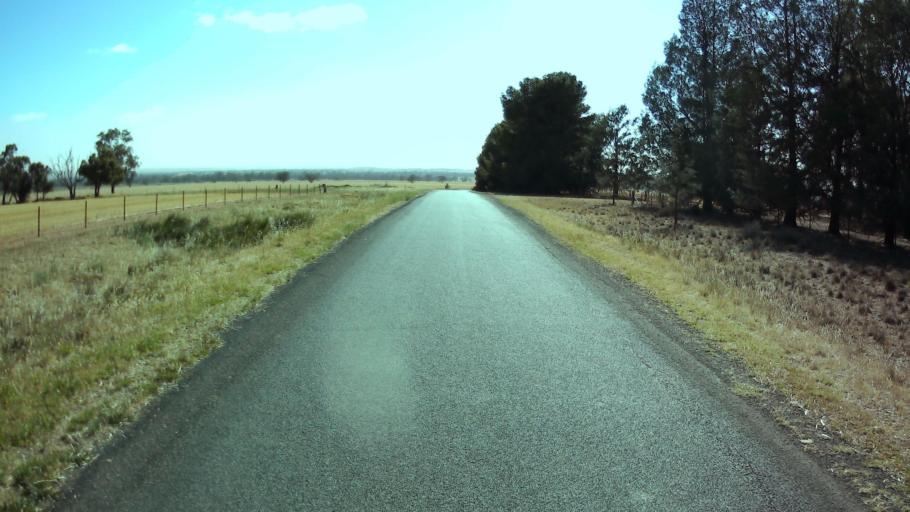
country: AU
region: New South Wales
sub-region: Weddin
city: Grenfell
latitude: -34.0622
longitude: 148.2658
